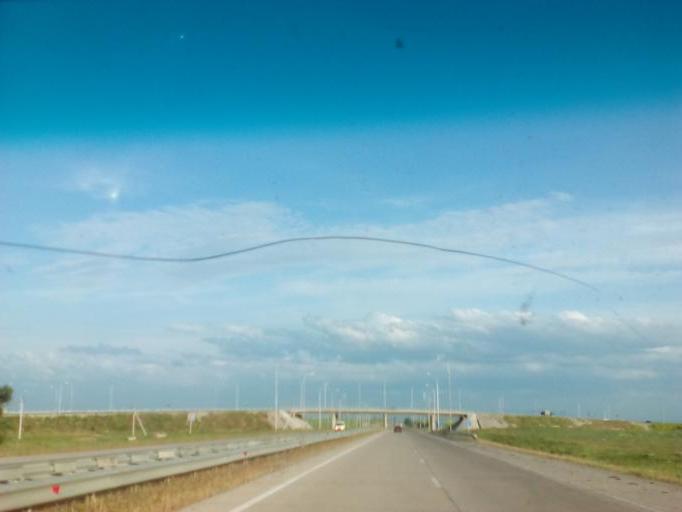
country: KZ
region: Ongtustik Qazaqstan
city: Temirlanovka
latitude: 42.5507
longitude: 69.3207
